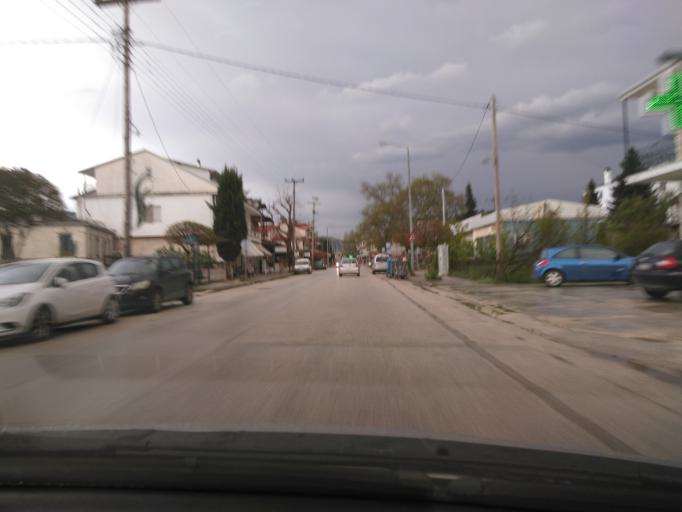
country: GR
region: Epirus
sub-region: Nomos Ioanninon
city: Katsikas
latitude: 39.6248
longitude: 20.8858
